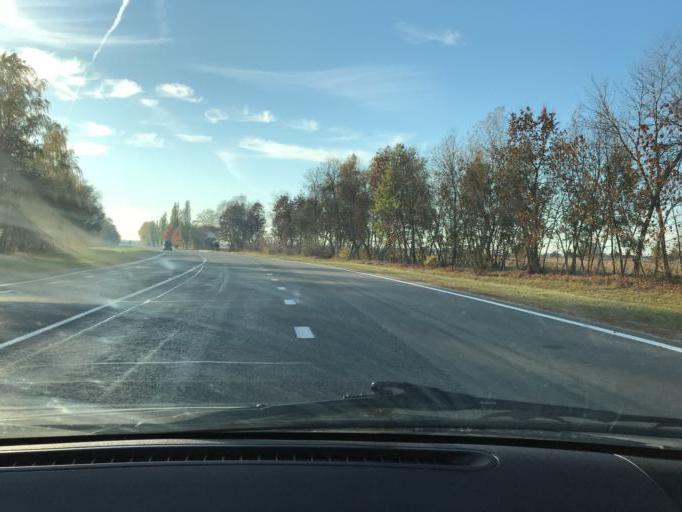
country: BY
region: Brest
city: Horad Kobryn
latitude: 52.2180
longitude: 24.5049
